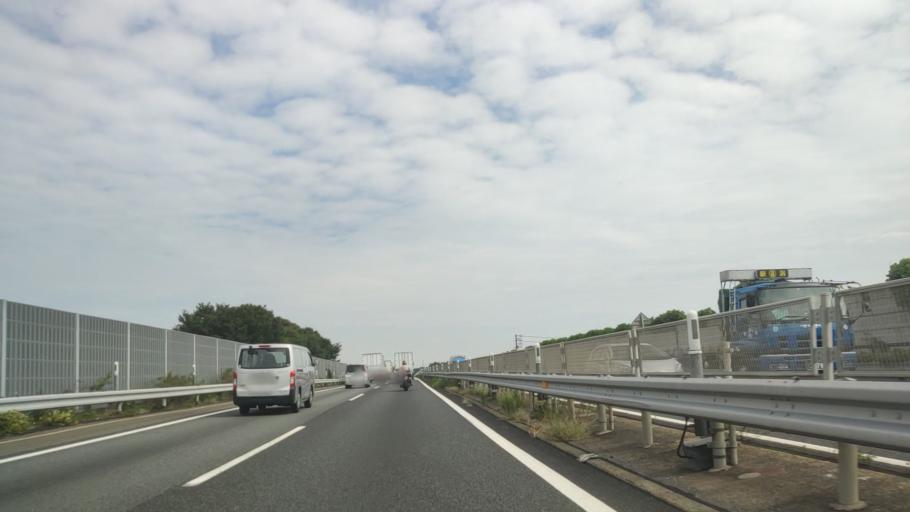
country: JP
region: Mie
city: Komono
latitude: 34.9427
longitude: 136.4935
